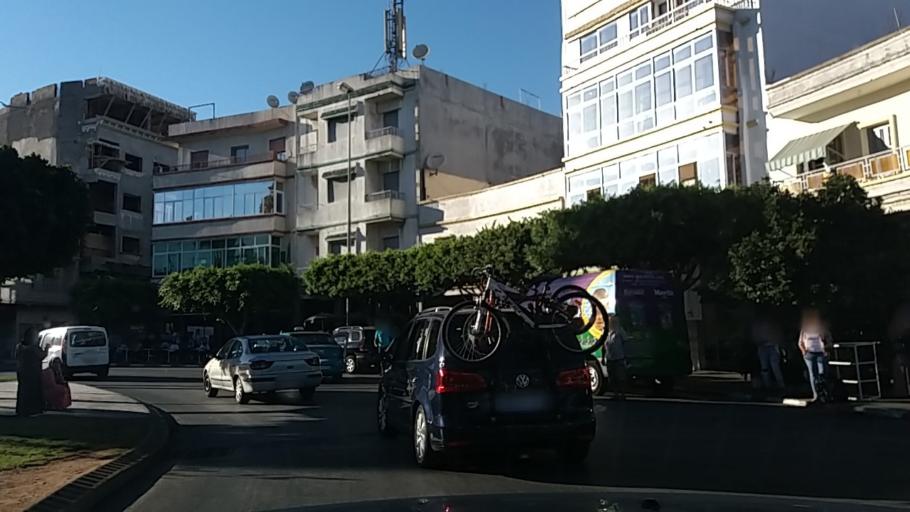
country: MA
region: Tanger-Tetouan
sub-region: Tanger-Assilah
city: Tangier
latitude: 35.7703
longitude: -5.8214
